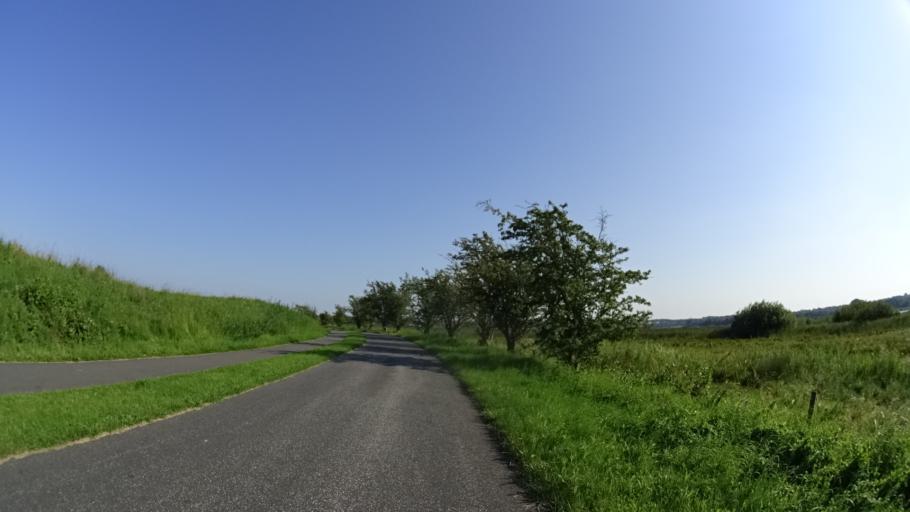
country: DK
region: Central Jutland
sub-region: Arhus Kommune
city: Stavtrup
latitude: 56.1455
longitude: 10.1334
